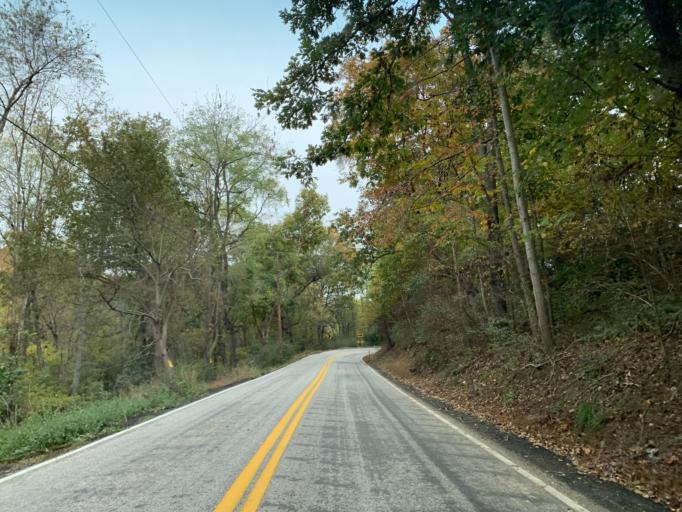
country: US
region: Pennsylvania
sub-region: York County
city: Susquehanna Trails
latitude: 39.7801
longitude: -76.4161
